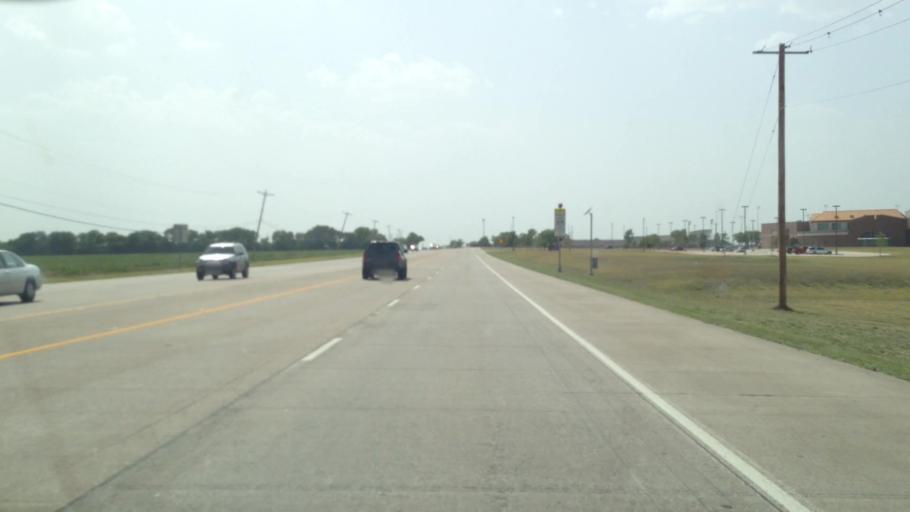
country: US
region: Texas
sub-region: Collin County
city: Princeton
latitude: 33.1724
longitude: -96.4829
